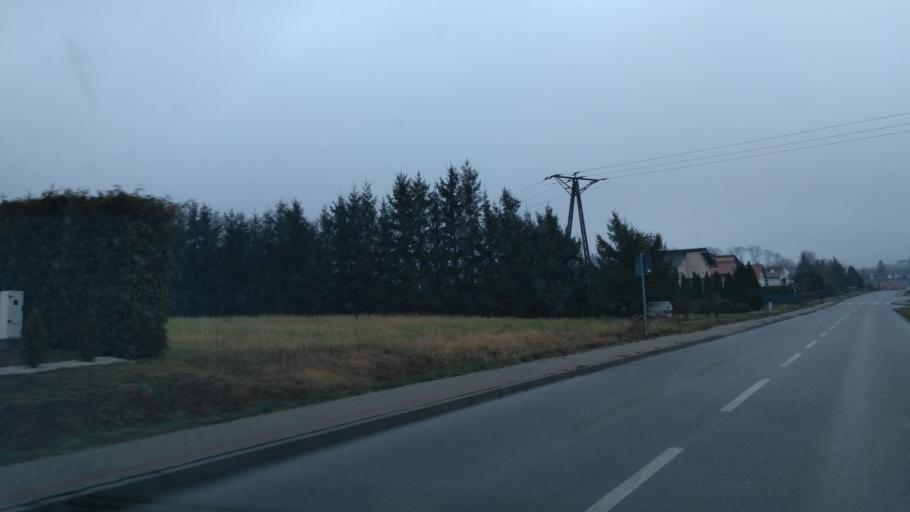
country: PL
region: Subcarpathian Voivodeship
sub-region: Powiat jaroslawski
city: Pruchnik
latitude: 49.9076
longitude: 22.5038
